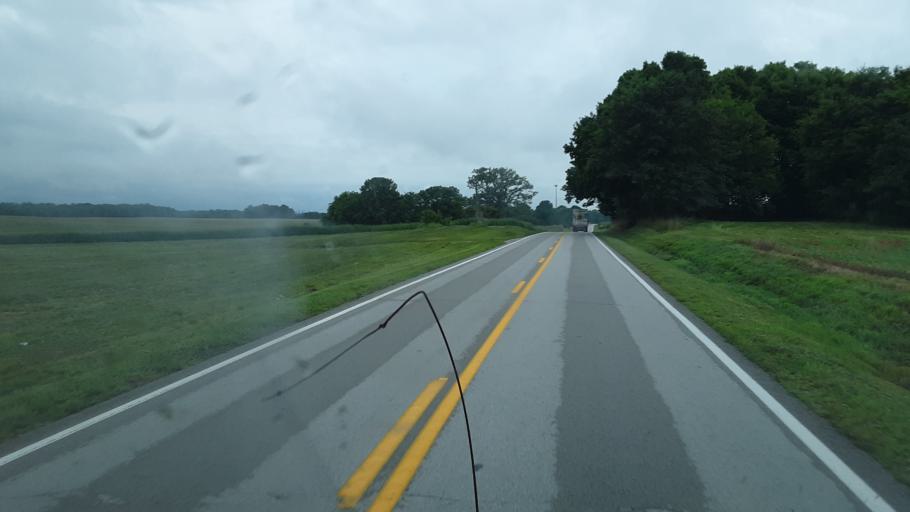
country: US
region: Kentucky
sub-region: Todd County
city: Elkton
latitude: 36.7489
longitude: -87.0464
